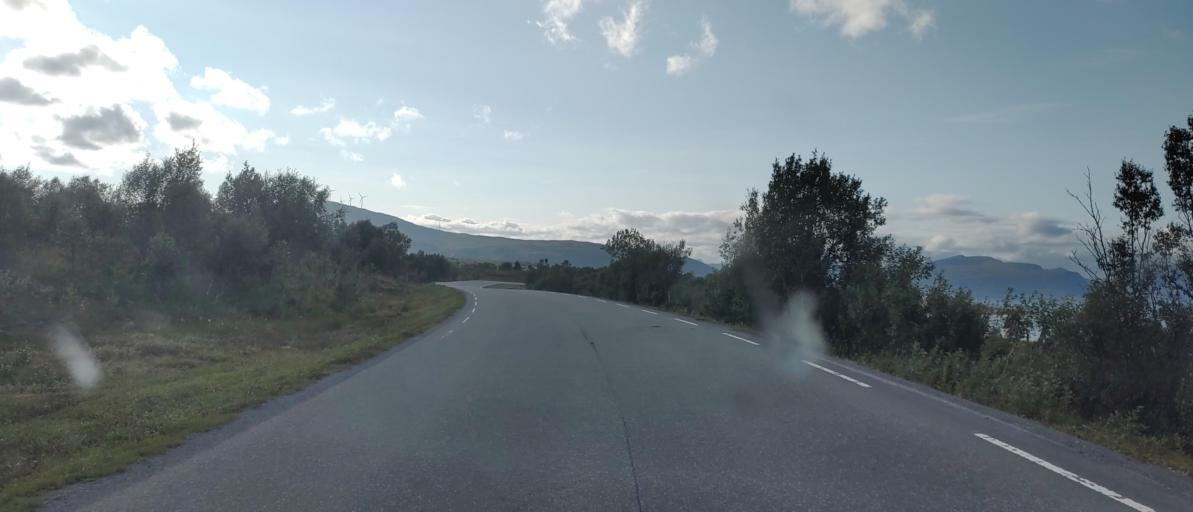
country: NO
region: Nordland
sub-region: Sortland
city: Sortland
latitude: 68.7229
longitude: 15.4921
